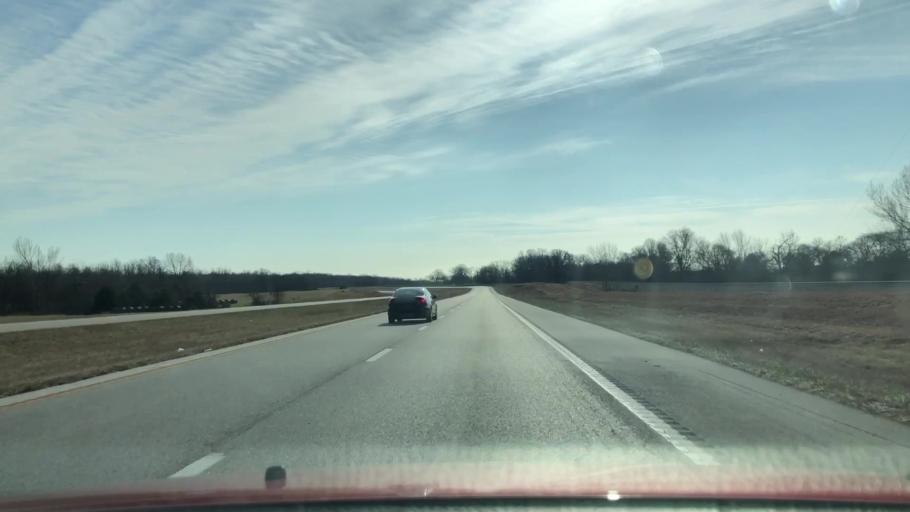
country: US
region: Missouri
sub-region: Webster County
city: Seymour
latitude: 37.1374
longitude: -92.7442
